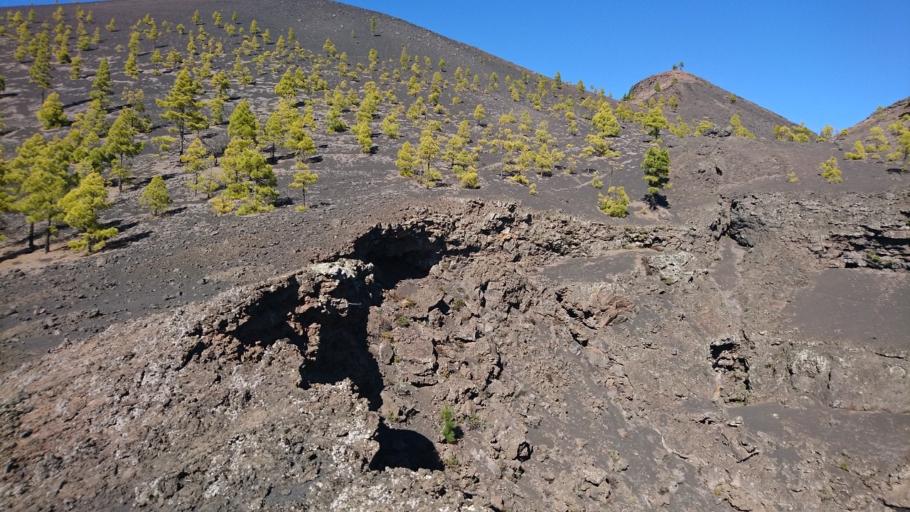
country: ES
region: Canary Islands
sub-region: Provincia de Santa Cruz de Tenerife
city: Fuencaliente de la Palma
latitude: 28.5328
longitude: -17.8382
